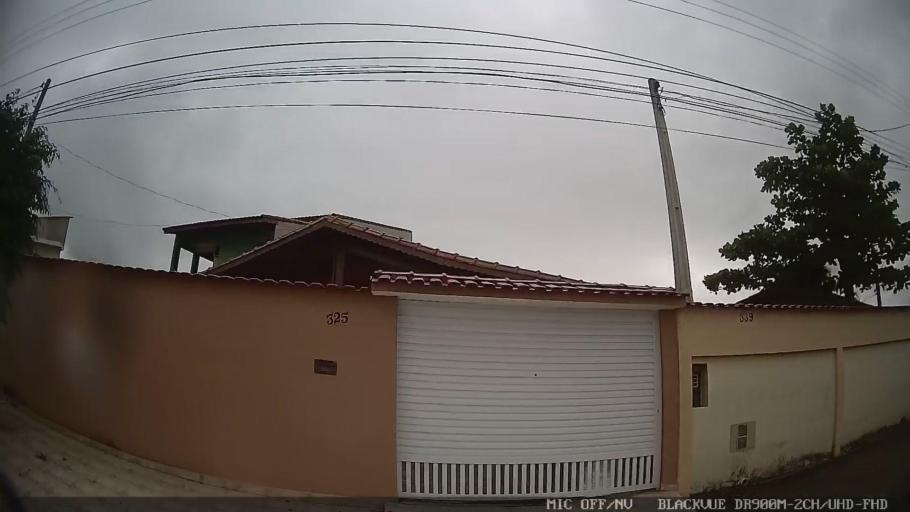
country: BR
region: Sao Paulo
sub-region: Itanhaem
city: Itanhaem
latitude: -24.1751
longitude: -46.7765
